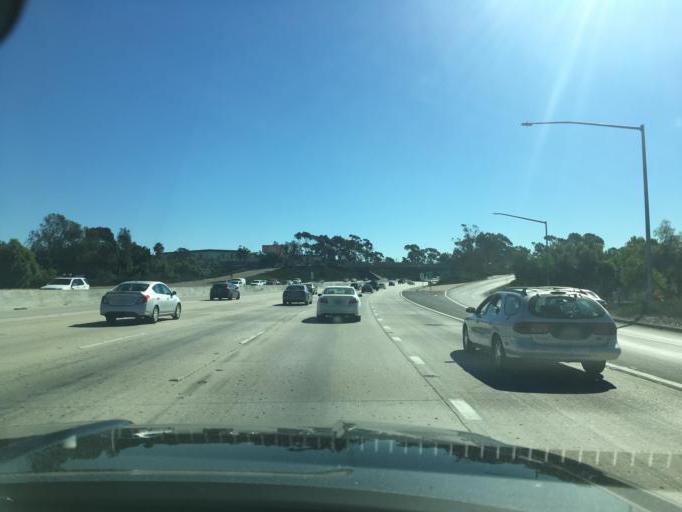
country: US
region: California
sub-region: San Diego County
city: National City
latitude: 32.7073
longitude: -117.0969
